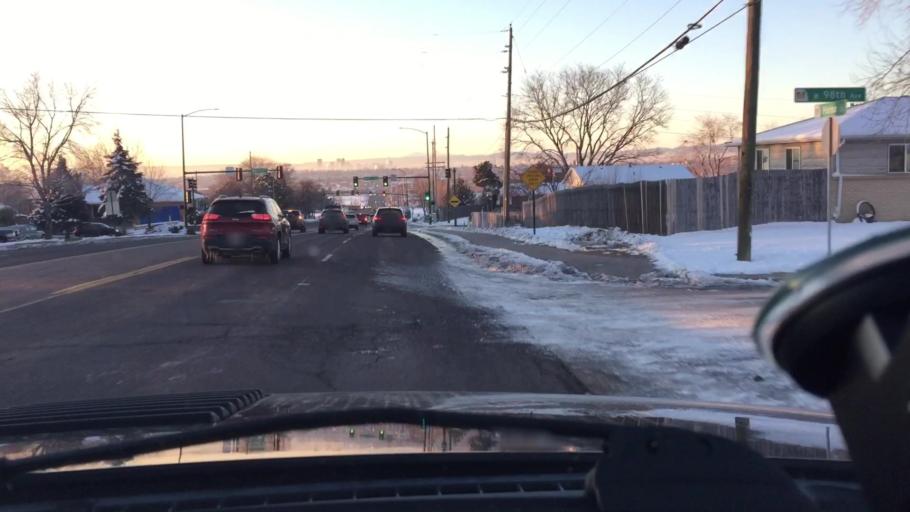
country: US
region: Colorado
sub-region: Adams County
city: Northglenn
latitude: 39.8735
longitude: -104.9967
